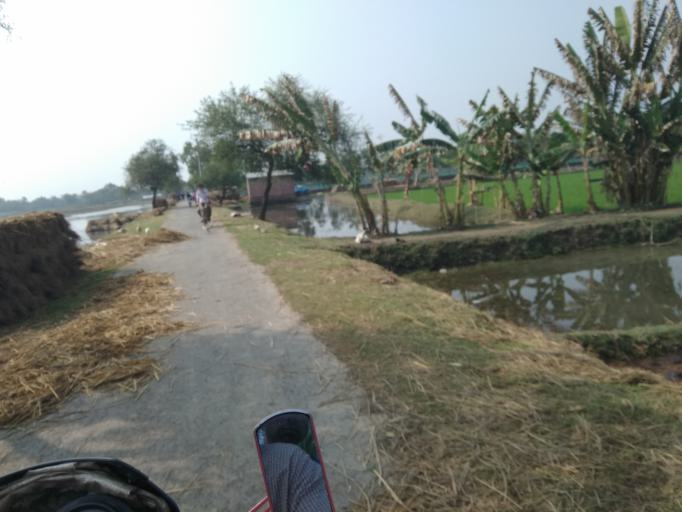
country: IN
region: West Bengal
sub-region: North 24 Parganas
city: Gosaba
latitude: 22.2616
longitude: 89.1154
